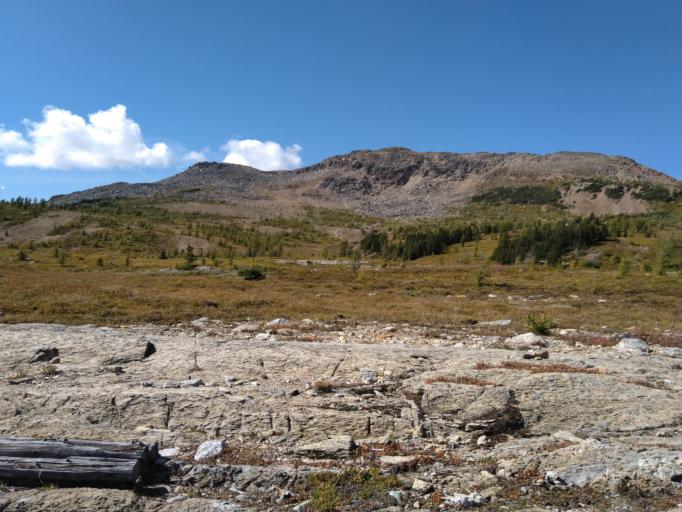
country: CA
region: Alberta
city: Banff
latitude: 51.0739
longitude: -115.7929
